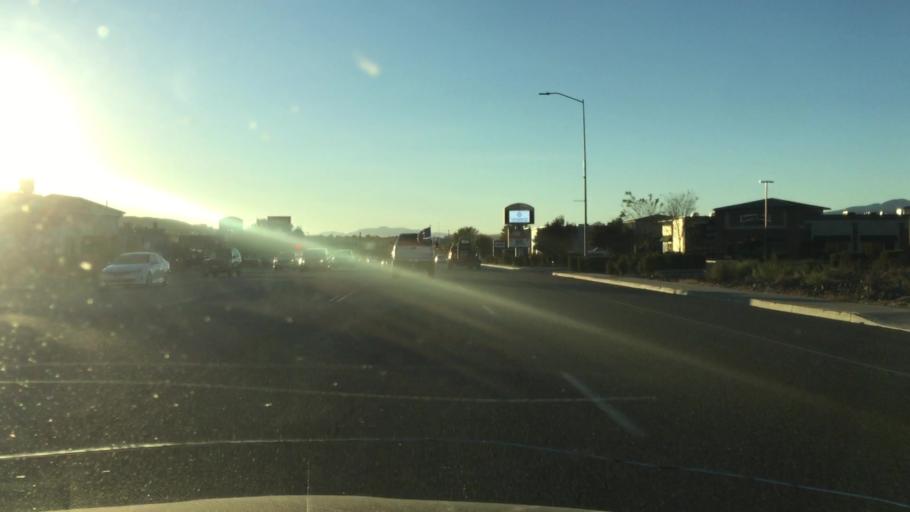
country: US
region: Utah
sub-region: Washington County
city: Hurricane
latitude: 37.1762
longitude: -113.3042
